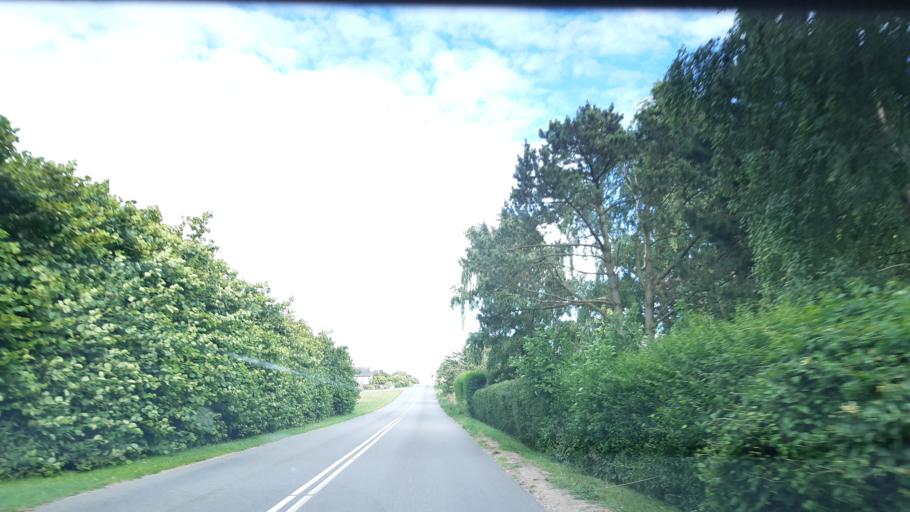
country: DK
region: Zealand
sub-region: Odsherred Kommune
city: Horve
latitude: 55.8186
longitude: 11.4128
